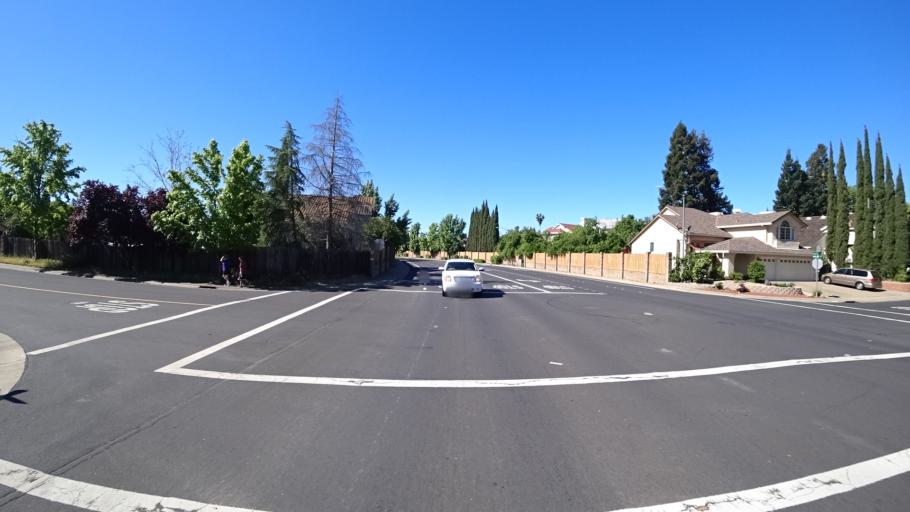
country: US
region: California
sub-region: Placer County
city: Rocklin
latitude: 38.7913
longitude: -121.2630
